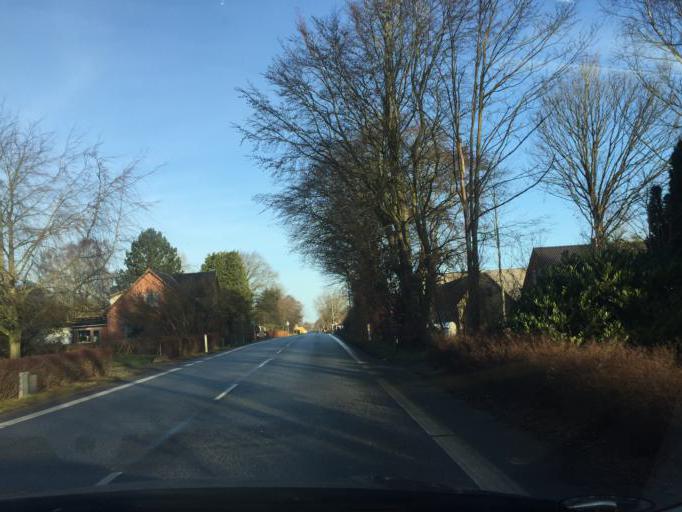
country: DK
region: South Denmark
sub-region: Middelfart Kommune
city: Ejby
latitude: 55.4414
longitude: 9.9440
